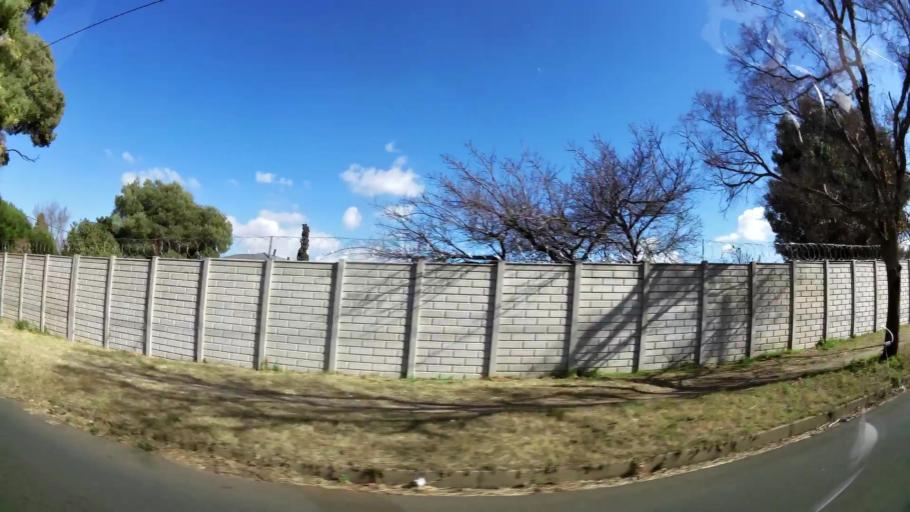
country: ZA
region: Gauteng
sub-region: City of Johannesburg Metropolitan Municipality
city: Roodepoort
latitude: -26.1405
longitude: 27.8357
